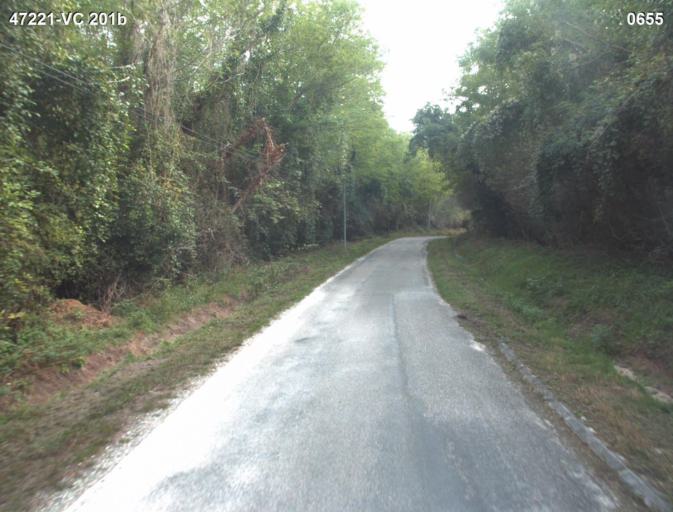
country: FR
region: Aquitaine
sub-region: Departement du Lot-et-Garonne
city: Mezin
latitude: 44.0798
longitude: 0.2415
